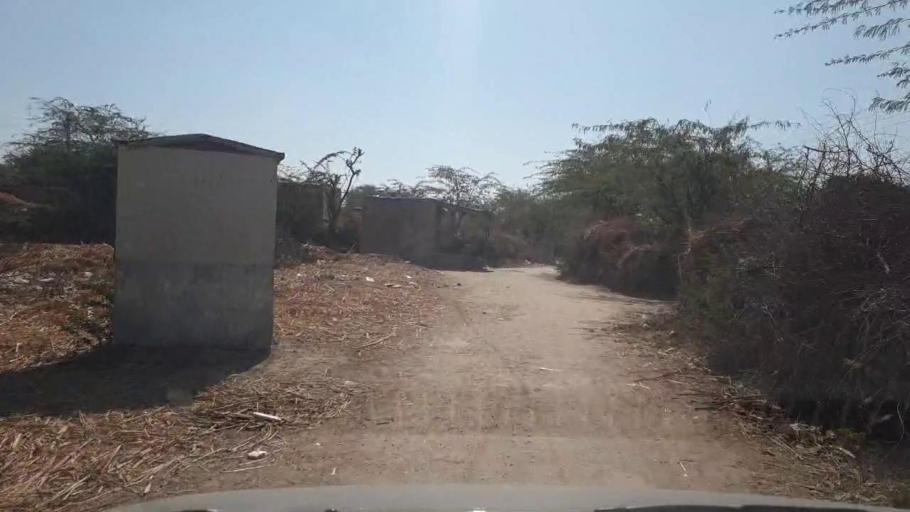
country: PK
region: Sindh
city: Samaro
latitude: 25.2699
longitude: 69.2667
